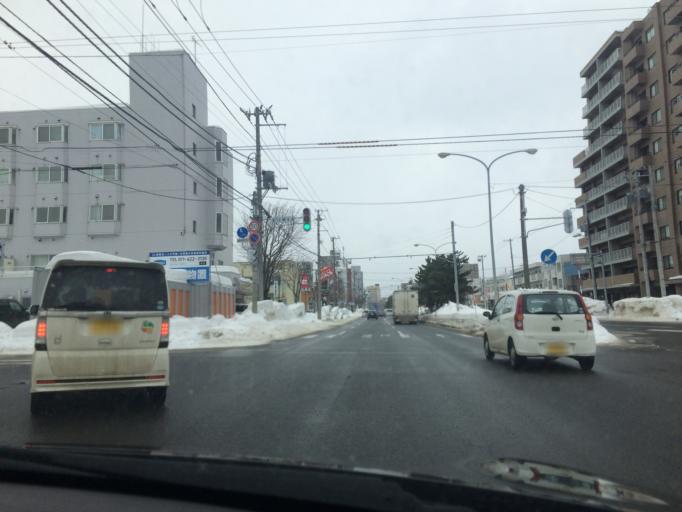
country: JP
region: Hokkaido
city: Sapporo
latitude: 43.0797
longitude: 141.3593
